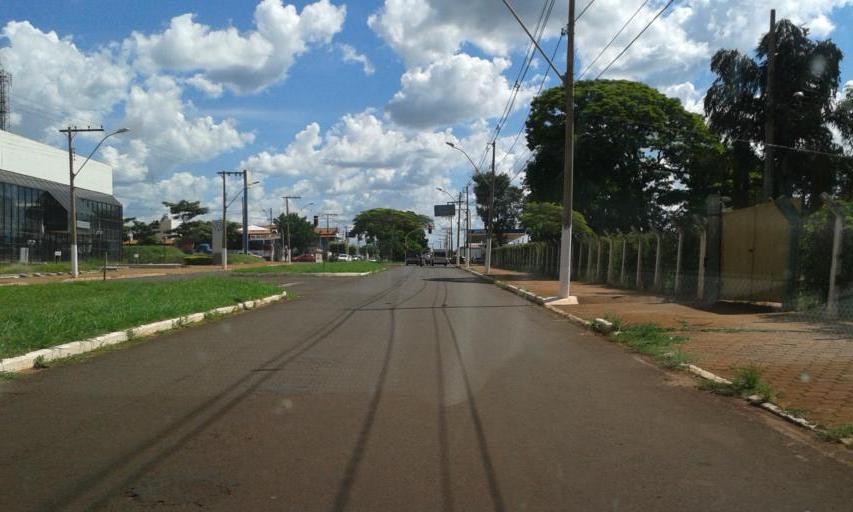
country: BR
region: Minas Gerais
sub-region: Ituiutaba
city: Ituiutaba
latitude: -18.9744
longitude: -49.4829
